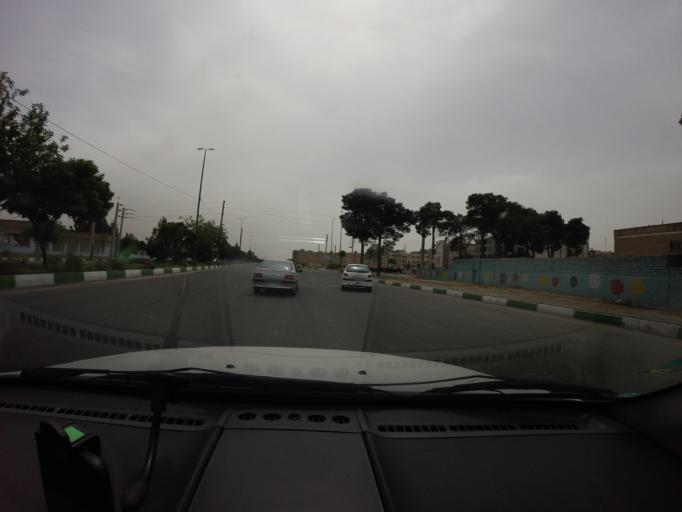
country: IR
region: Tehran
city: Eslamshahr
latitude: 35.5390
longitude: 51.2222
